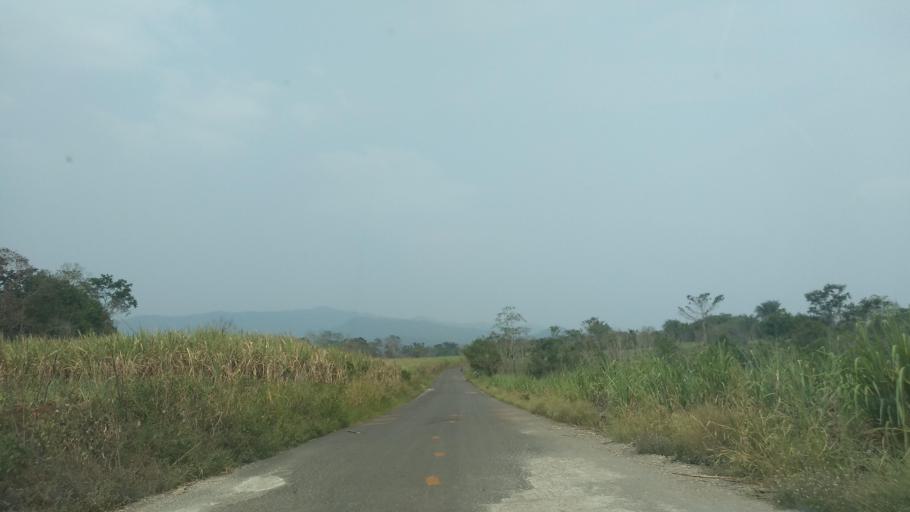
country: MX
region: Veracruz
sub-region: Tezonapa
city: Laguna Chica (Pueblo Nuevo)
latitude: 18.5447
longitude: -96.7569
